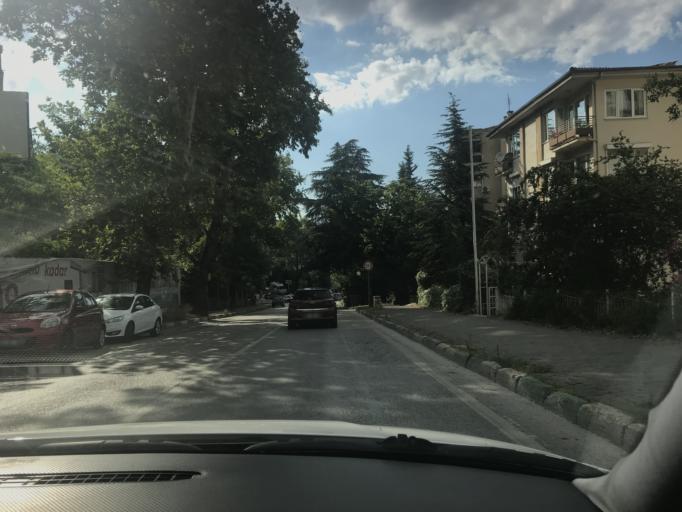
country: TR
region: Bursa
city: Yildirim
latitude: 40.2037
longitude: 29.0218
